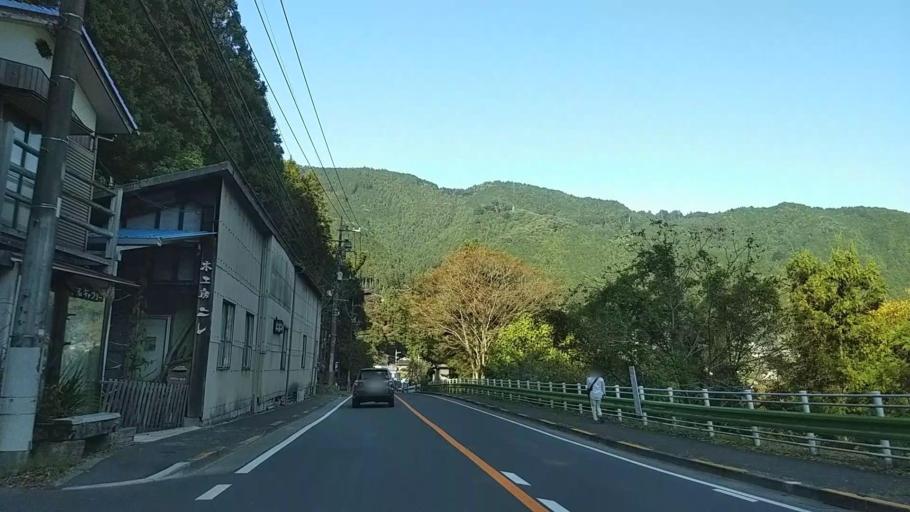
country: JP
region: Tokyo
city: Ome
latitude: 35.8028
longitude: 139.1851
